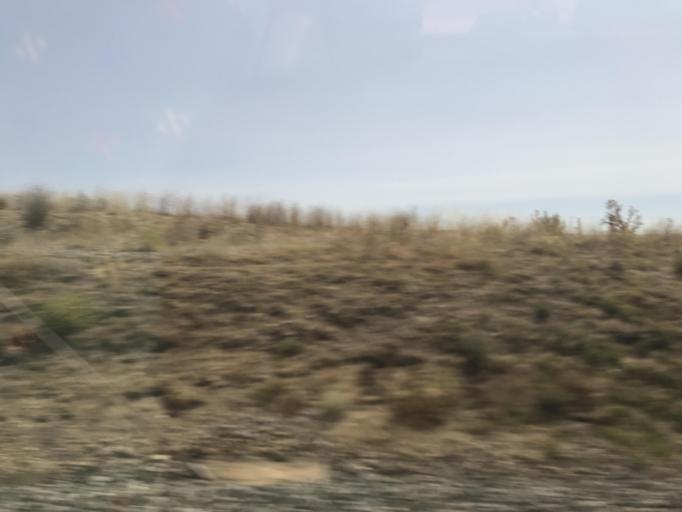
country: ES
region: Castille and Leon
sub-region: Provincia de Burgos
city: Villazopeque
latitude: 42.1927
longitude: -4.0267
